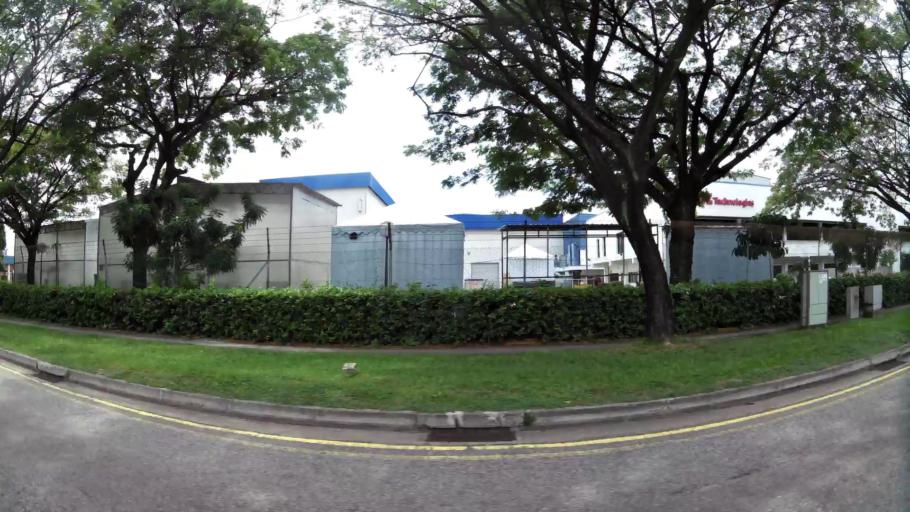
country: MY
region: Johor
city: Johor Bahru
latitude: 1.3221
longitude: 103.6733
